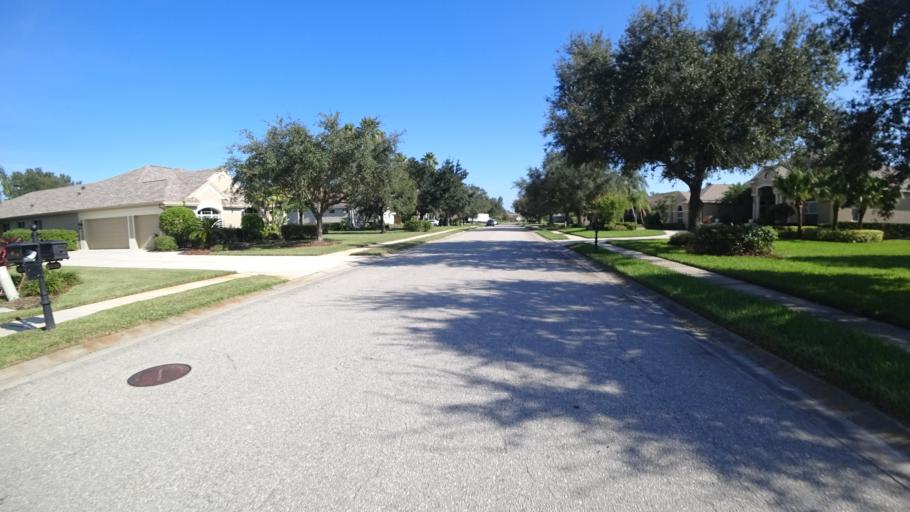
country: US
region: Florida
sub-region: Sarasota County
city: The Meadows
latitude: 27.4077
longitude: -82.4435
